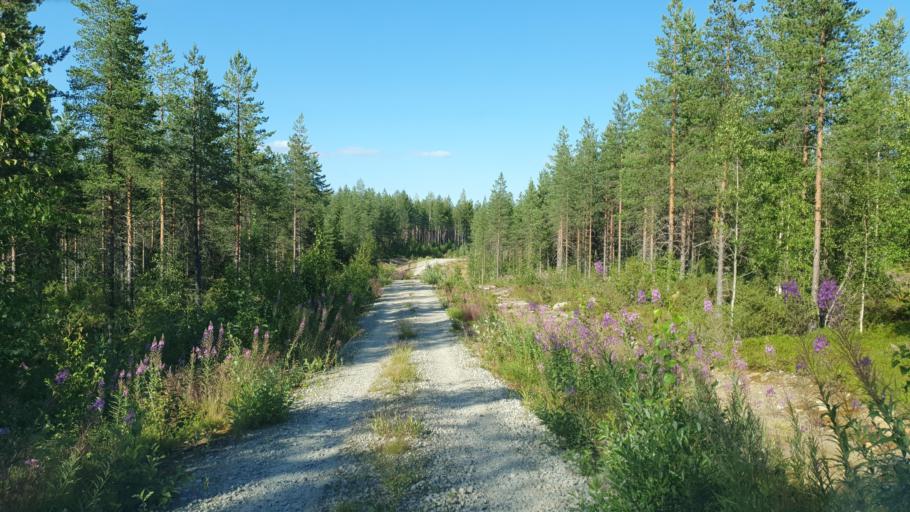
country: FI
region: Kainuu
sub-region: Kehys-Kainuu
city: Kuhmo
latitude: 64.0017
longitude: 29.7516
